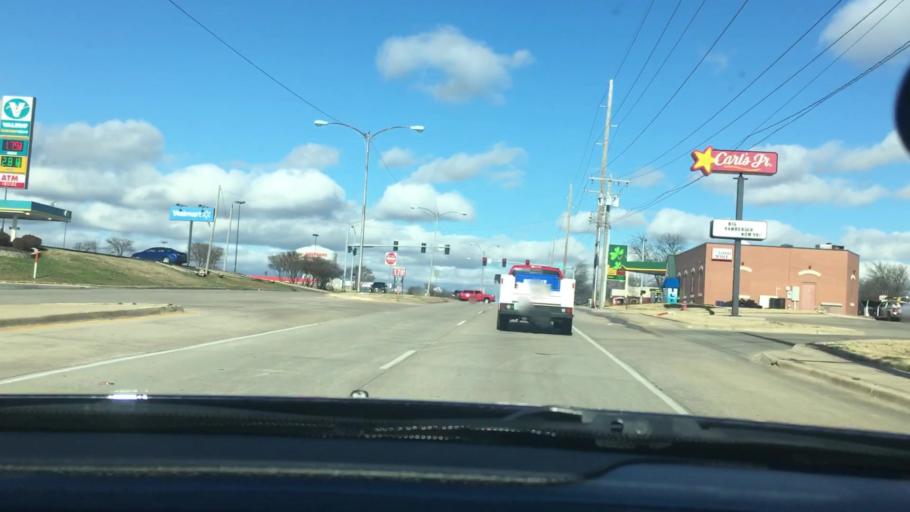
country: US
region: Oklahoma
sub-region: Carter County
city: Ardmore
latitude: 34.1917
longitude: -97.1430
